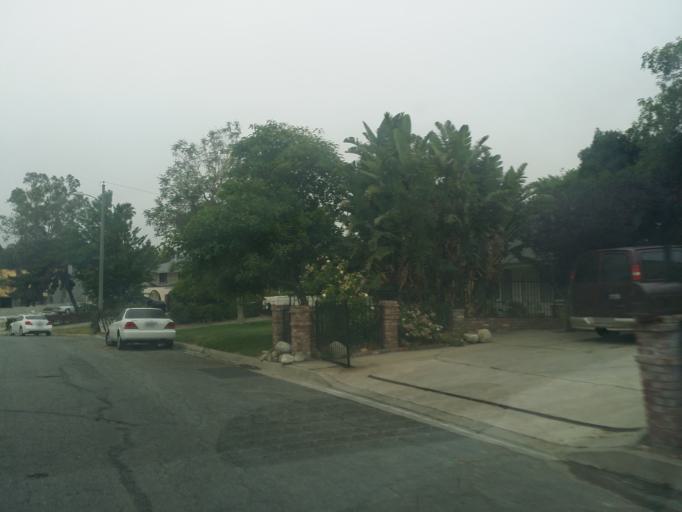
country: US
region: California
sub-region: San Bernardino County
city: Muscoy
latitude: 34.1454
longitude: -117.3789
